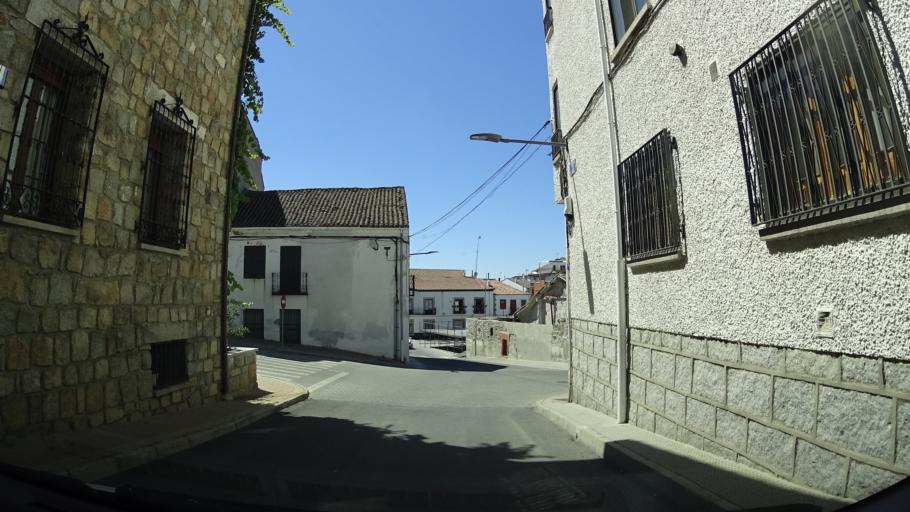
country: ES
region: Castille and Leon
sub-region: Provincia de Avila
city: Las Navas del Marques
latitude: 40.6044
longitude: -4.3276
